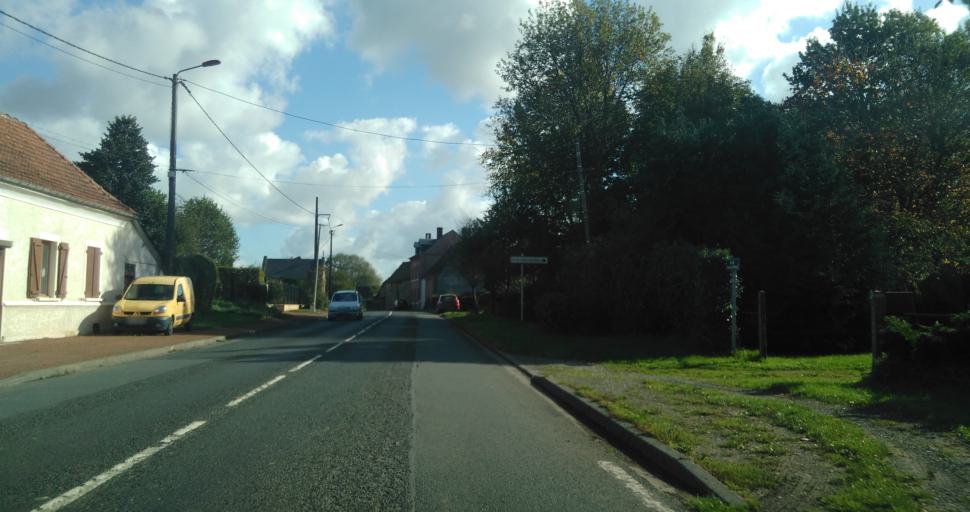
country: FR
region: Picardie
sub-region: Departement de la Somme
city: Bernaville
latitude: 50.1414
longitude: 2.1152
